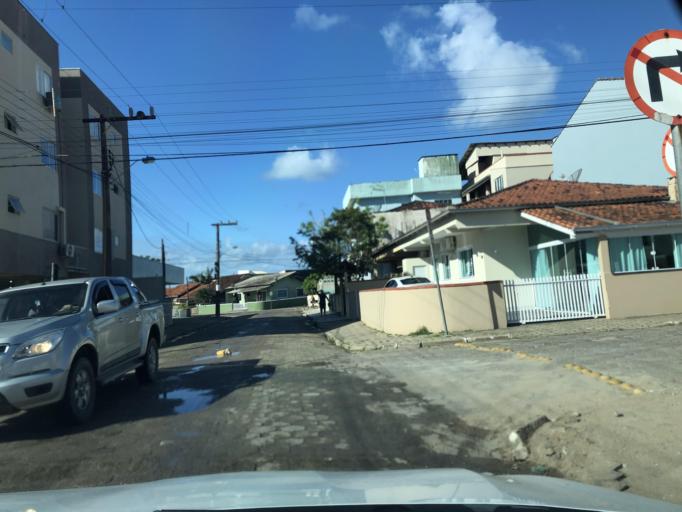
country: BR
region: Santa Catarina
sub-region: Sao Francisco Do Sul
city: Sao Francisco do Sul
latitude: -26.2297
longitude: -48.5045
